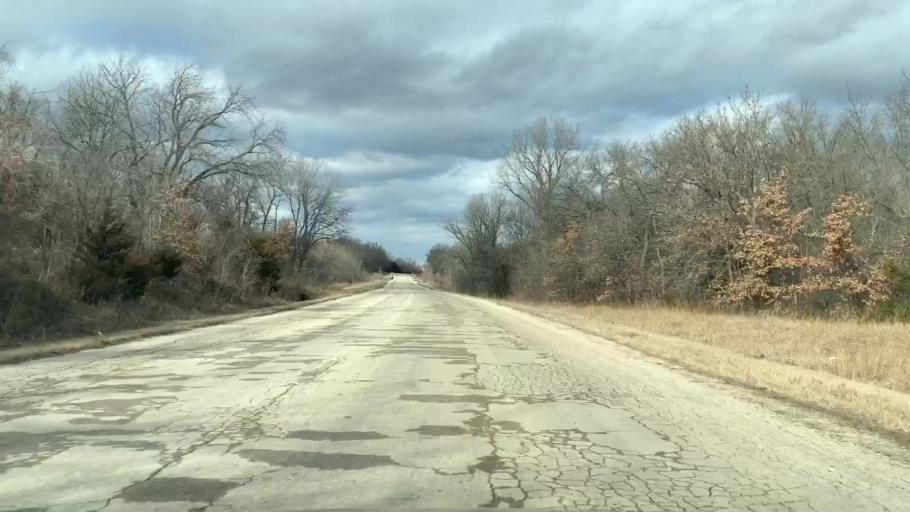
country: US
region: Kansas
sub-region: Allen County
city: Humboldt
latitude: 37.7503
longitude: -95.4704
